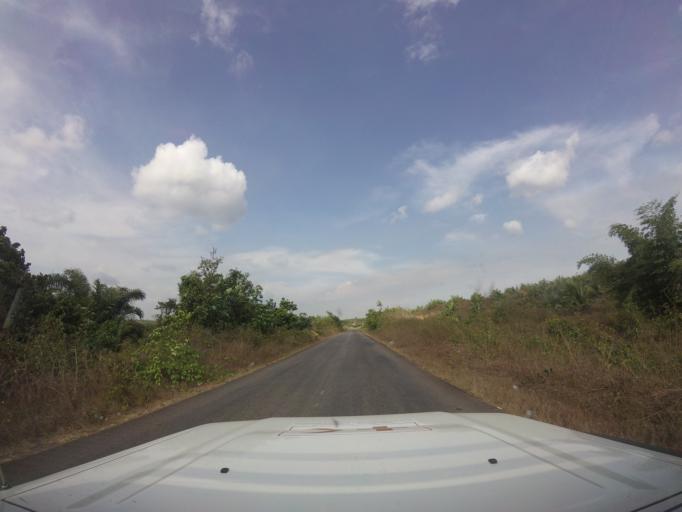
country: LR
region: Bomi
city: Tubmanburg
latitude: 6.7129
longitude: -10.9422
